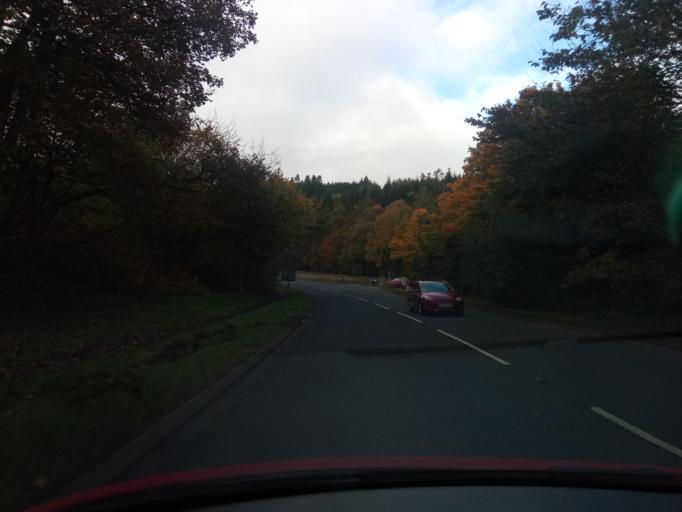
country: GB
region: Scotland
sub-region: The Scottish Borders
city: Galashiels
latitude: 55.6297
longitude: -2.8410
